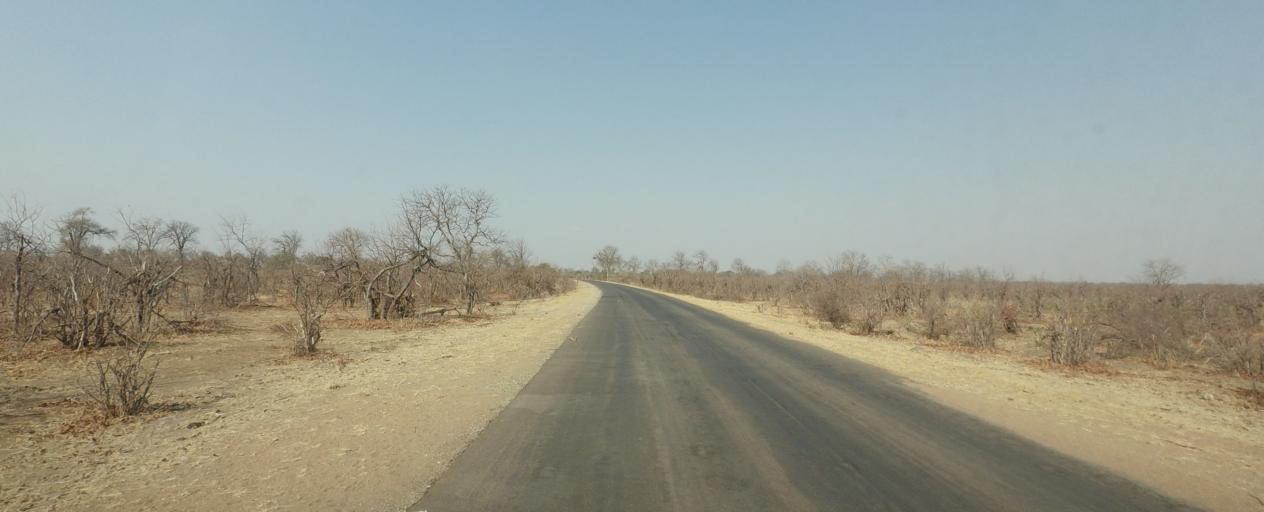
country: ZA
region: Limpopo
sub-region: Mopani District Municipality
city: Giyani
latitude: -23.0978
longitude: 31.4106
